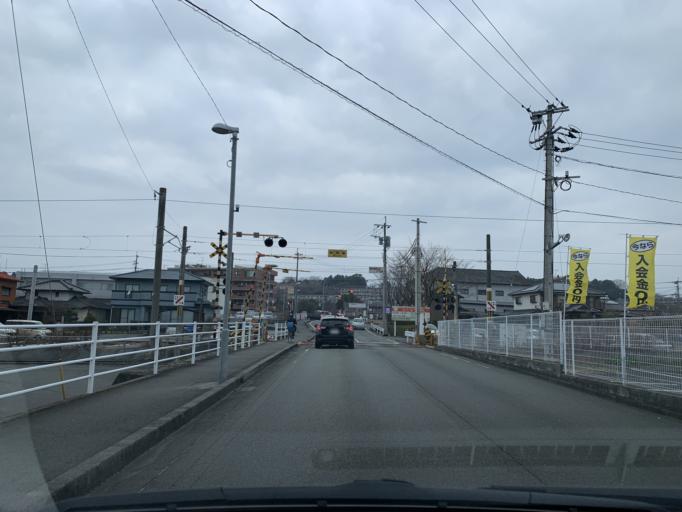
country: JP
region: Kumamoto
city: Ozu
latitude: 32.8767
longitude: 130.8579
